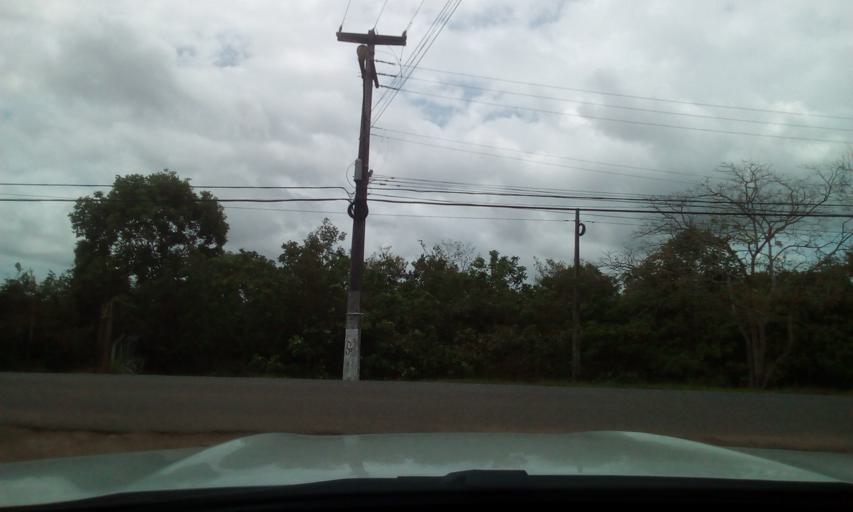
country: BR
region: Paraiba
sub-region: Bayeux
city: Bayeux
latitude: -7.1406
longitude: -34.9481
